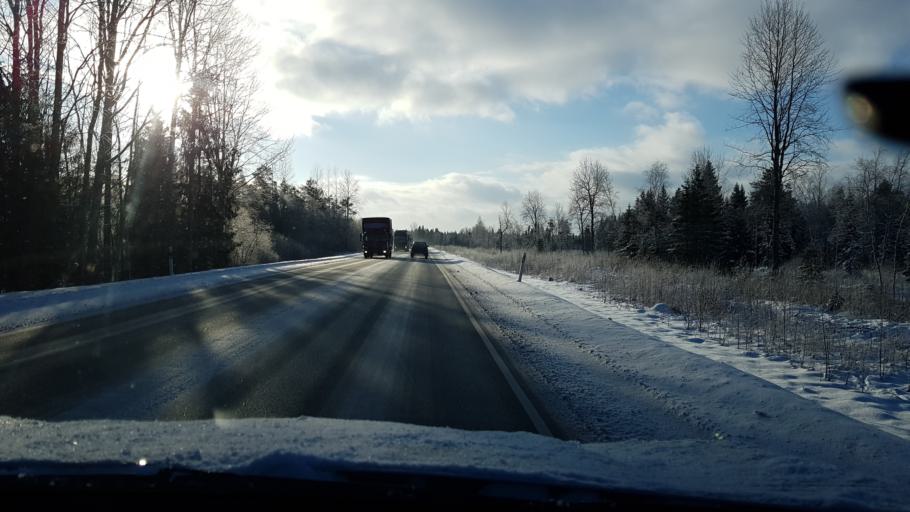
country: EE
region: Harju
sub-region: Nissi vald
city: Riisipere
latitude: 59.1640
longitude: 24.3466
